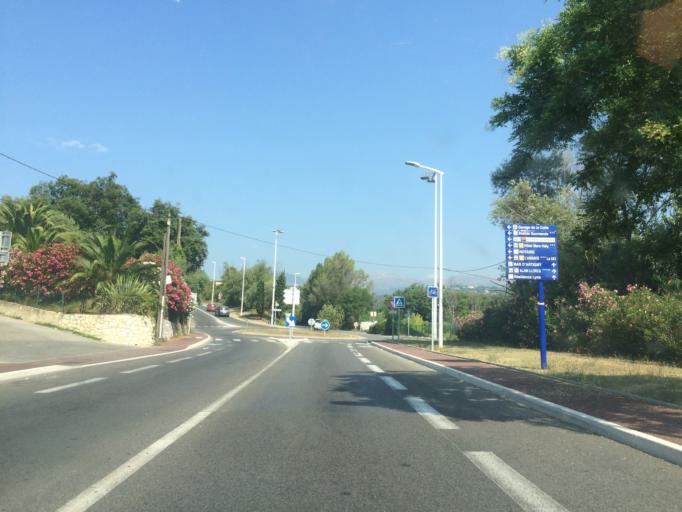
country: FR
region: Provence-Alpes-Cote d'Azur
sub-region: Departement des Alpes-Maritimes
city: La Colle-sur-Loup
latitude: 43.6832
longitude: 7.1159
